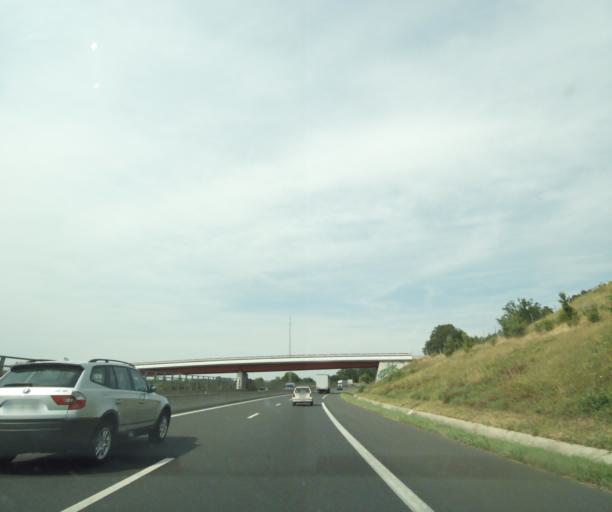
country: FR
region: Centre
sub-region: Departement d'Indre-et-Loire
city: La Membrolle-sur-Choisille
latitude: 47.4238
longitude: 0.6352
